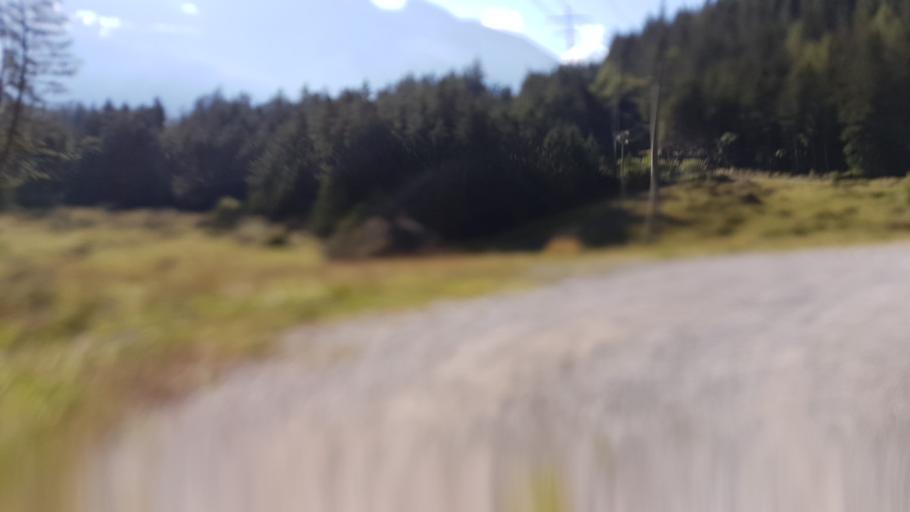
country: CH
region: Bern
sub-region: Frutigen-Niedersimmental District
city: Kandersteg
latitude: 46.5102
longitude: 7.6714
